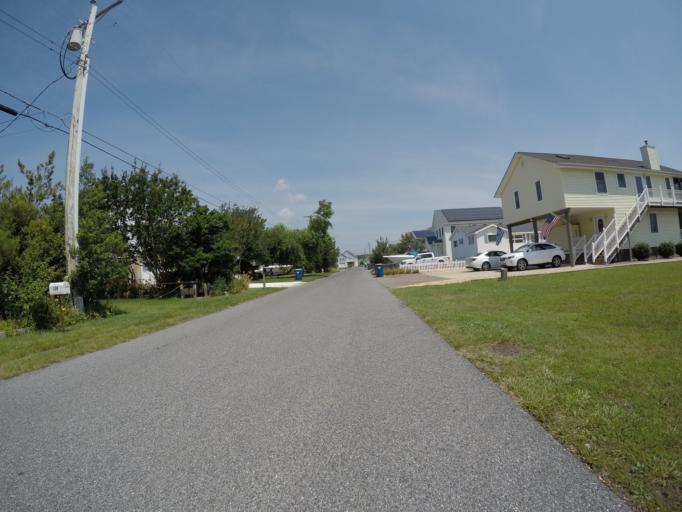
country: US
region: Delaware
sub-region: Sussex County
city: Bethany Beach
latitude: 38.5138
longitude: -75.0565
